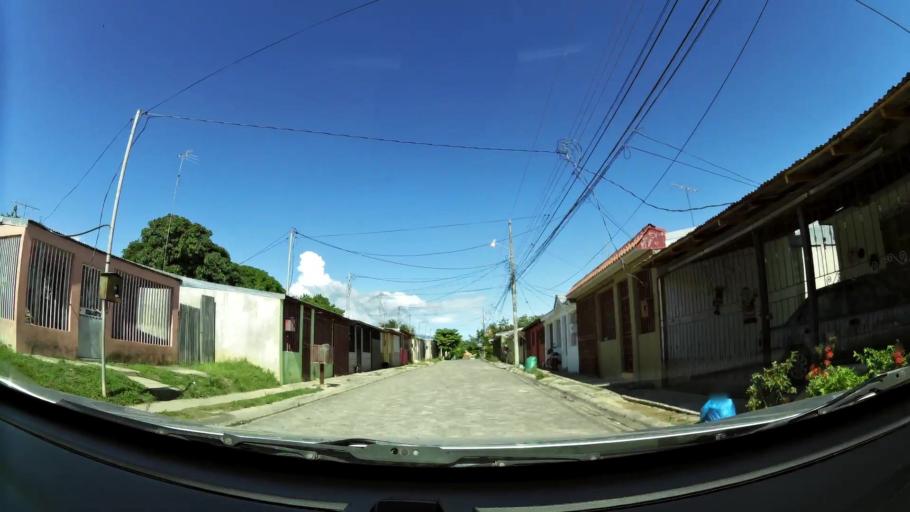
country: CR
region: Guanacaste
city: Liberia
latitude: 10.6380
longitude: -85.4387
